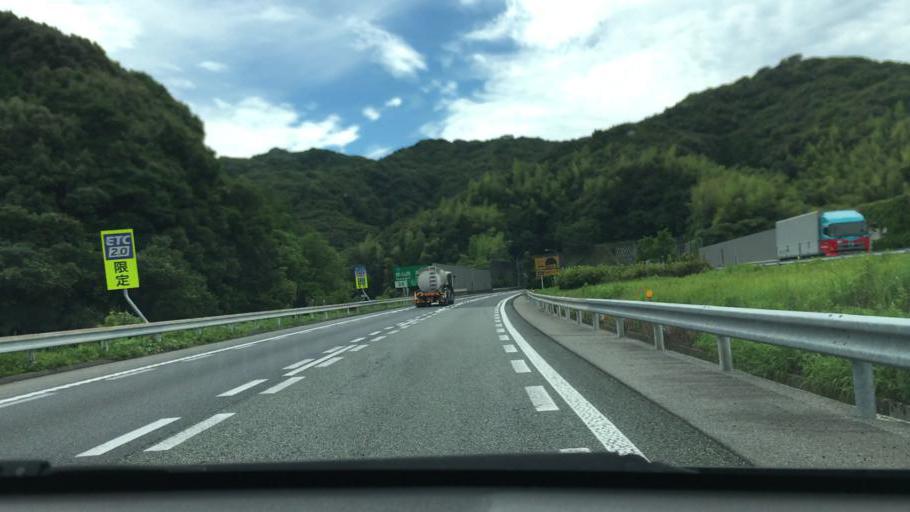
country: JP
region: Yamaguchi
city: Tokuyama
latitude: 34.0661
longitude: 131.6981
